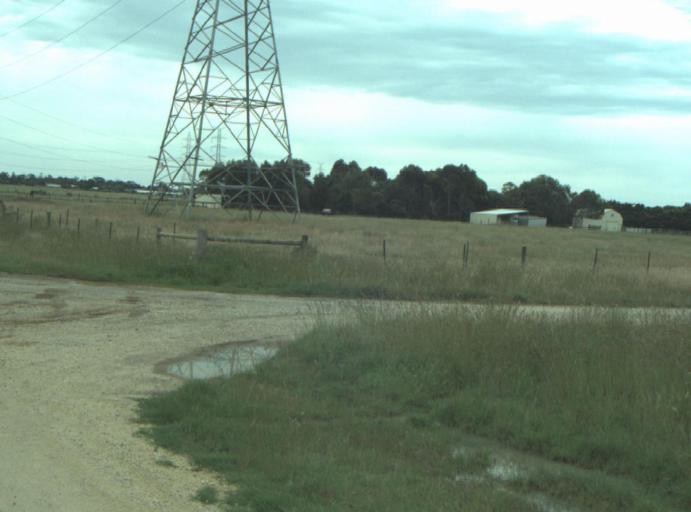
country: AU
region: Victoria
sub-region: Greater Geelong
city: Breakwater
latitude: -38.1996
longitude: 144.3977
